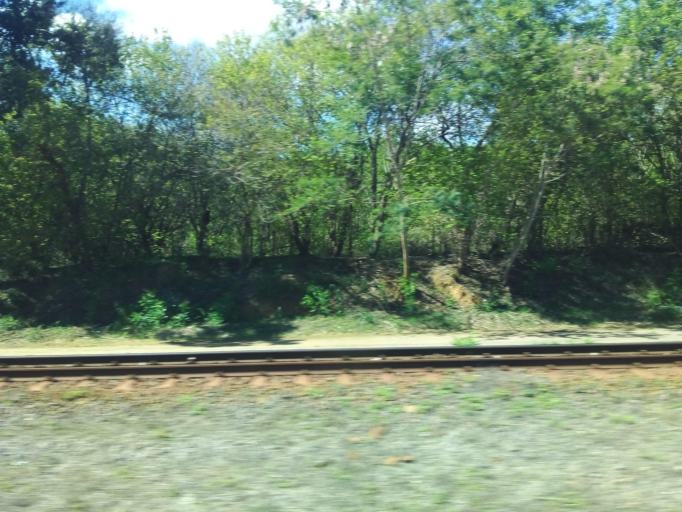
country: BR
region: Minas Gerais
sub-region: Governador Valadares
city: Governador Valadares
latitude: -18.8376
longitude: -41.8837
